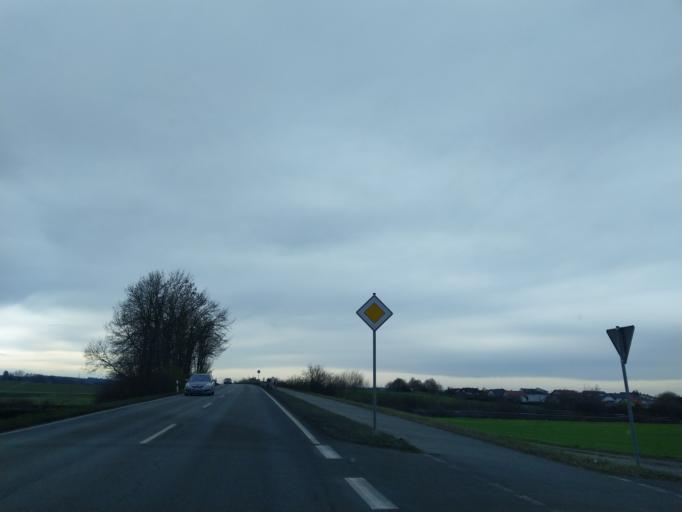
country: DE
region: Bavaria
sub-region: Lower Bavaria
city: Osterhofen
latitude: 48.6883
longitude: 13.0351
